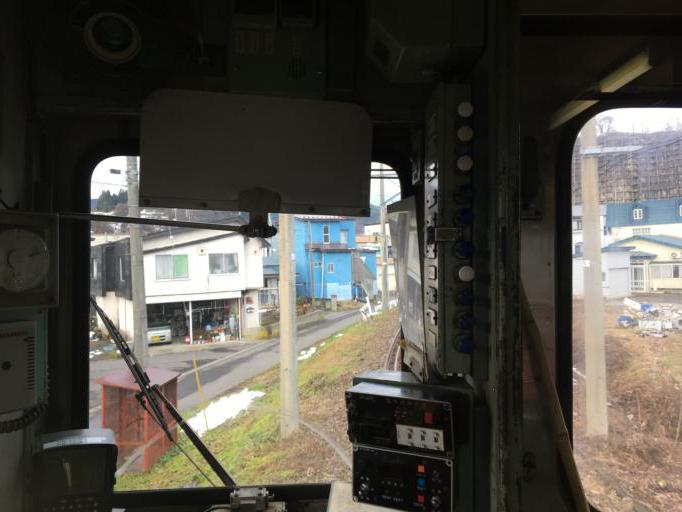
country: JP
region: Aomori
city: Hirosaki
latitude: 40.5219
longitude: 140.5648
